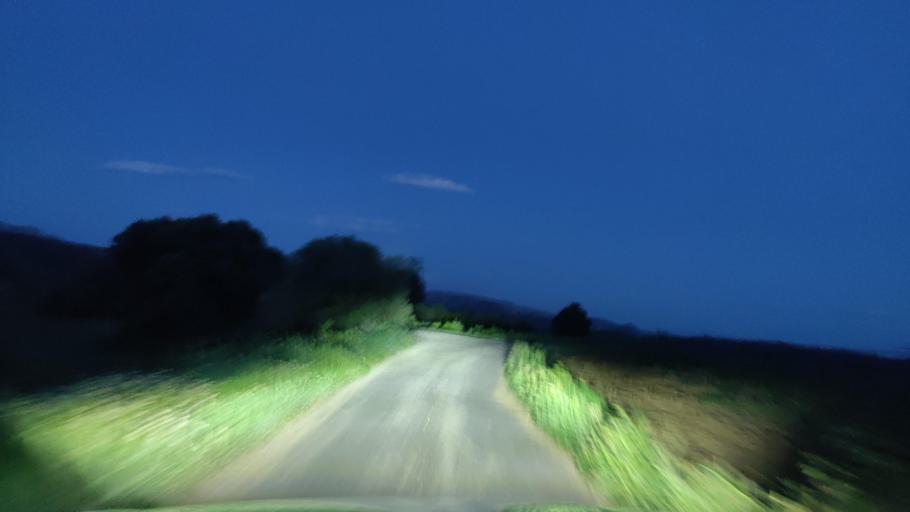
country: FR
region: Languedoc-Roussillon
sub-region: Departement des Pyrenees-Orientales
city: Estagel
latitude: 42.8806
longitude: 2.7265
